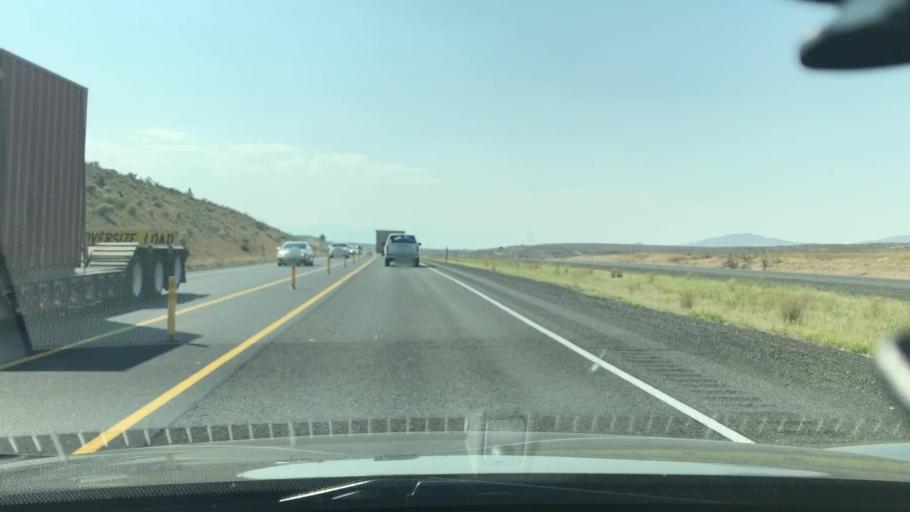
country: US
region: Oregon
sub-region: Baker County
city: Baker City
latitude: 44.6850
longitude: -117.6658
